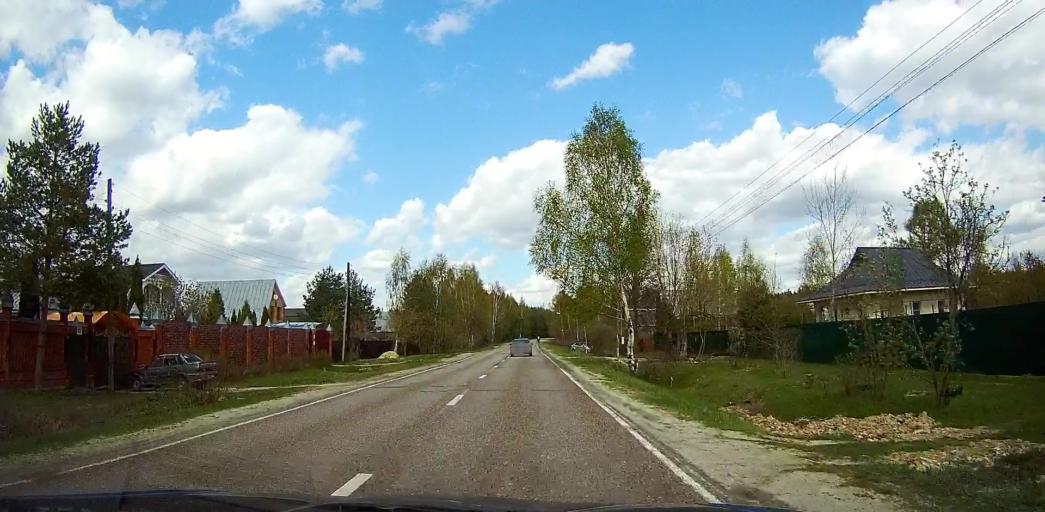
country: RU
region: Moskovskaya
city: Davydovo
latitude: 55.5885
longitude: 38.8305
